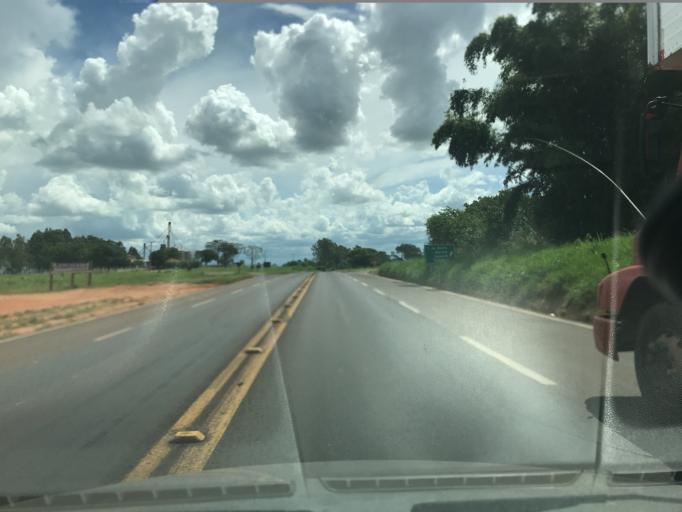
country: BR
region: Parana
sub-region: Cruzeiro Do Oeste
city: Cruzeiro do Oeste
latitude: -23.7985
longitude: -53.0546
